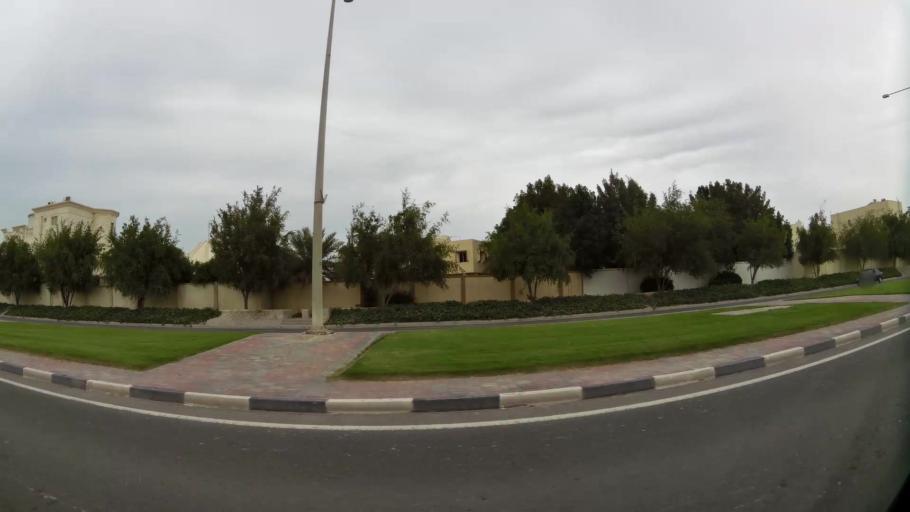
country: QA
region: Baladiyat ad Dawhah
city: Doha
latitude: 25.3383
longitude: 51.5059
